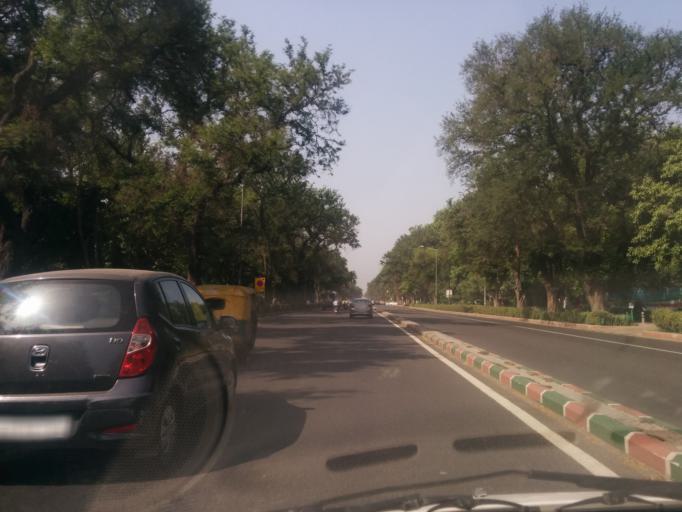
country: IN
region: NCT
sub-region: New Delhi
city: New Delhi
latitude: 28.6227
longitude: 77.2385
